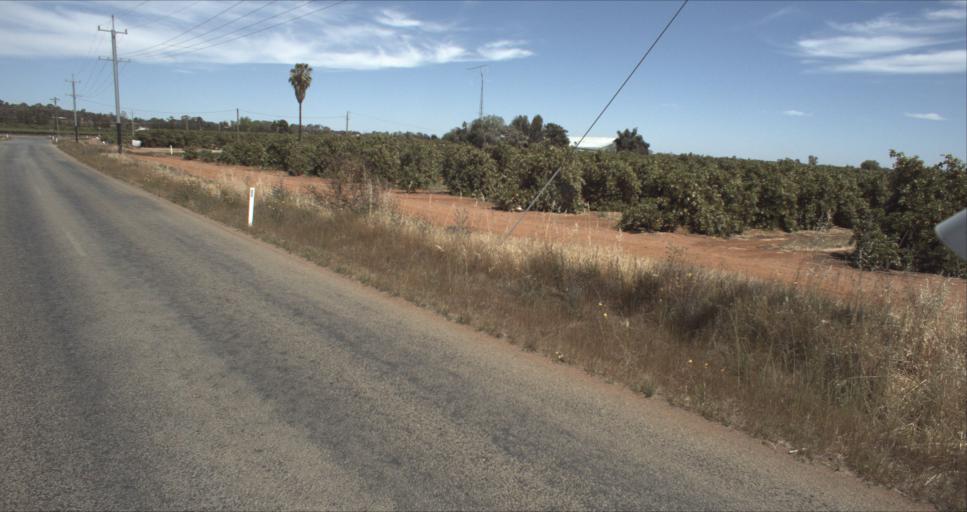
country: AU
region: New South Wales
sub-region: Leeton
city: Leeton
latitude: -34.5636
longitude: 146.4523
